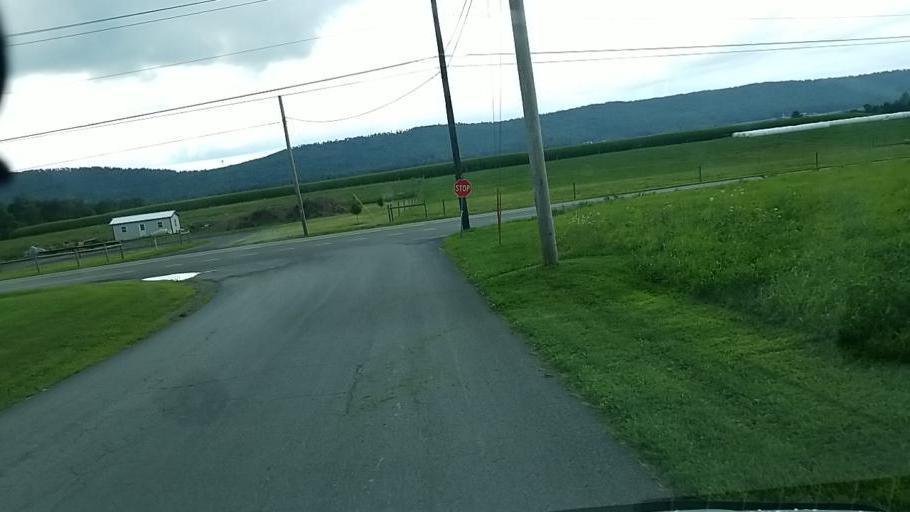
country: US
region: Pennsylvania
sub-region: Dauphin County
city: Elizabethville
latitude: 40.5837
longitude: -76.8619
